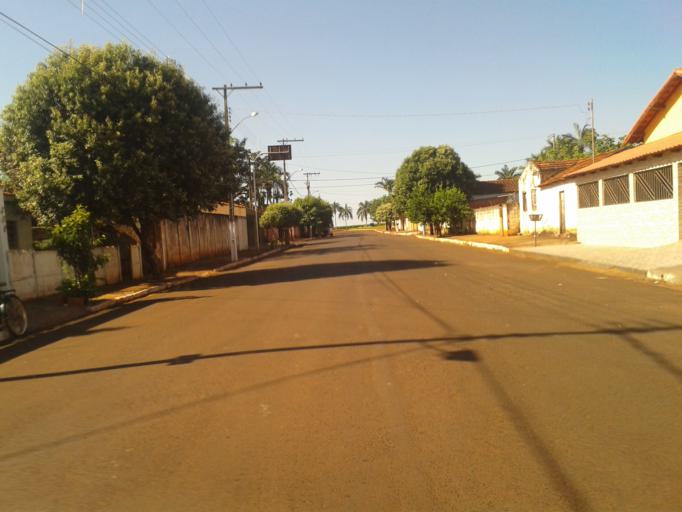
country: BR
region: Minas Gerais
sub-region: Santa Vitoria
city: Santa Vitoria
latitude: -18.6946
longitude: -49.9405
